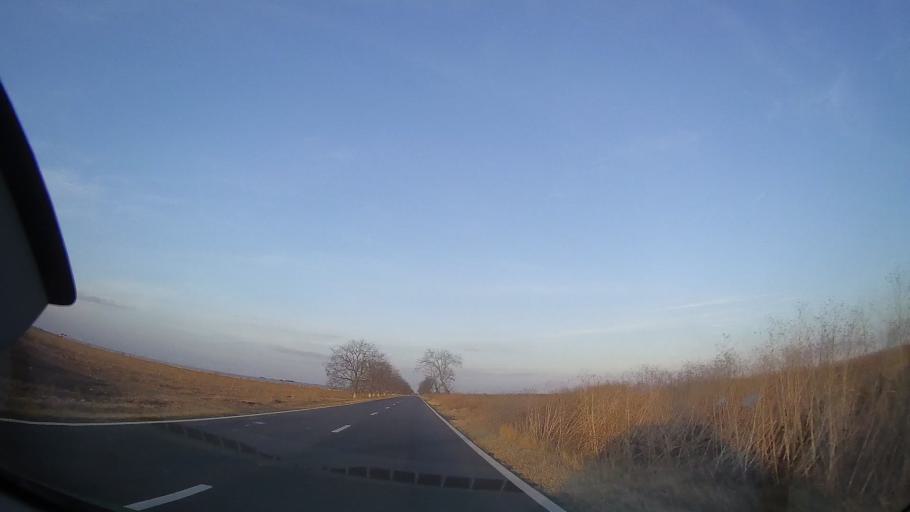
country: RO
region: Constanta
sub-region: Comuna Topraisar
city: Topraisar
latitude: 43.9937
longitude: 28.4276
